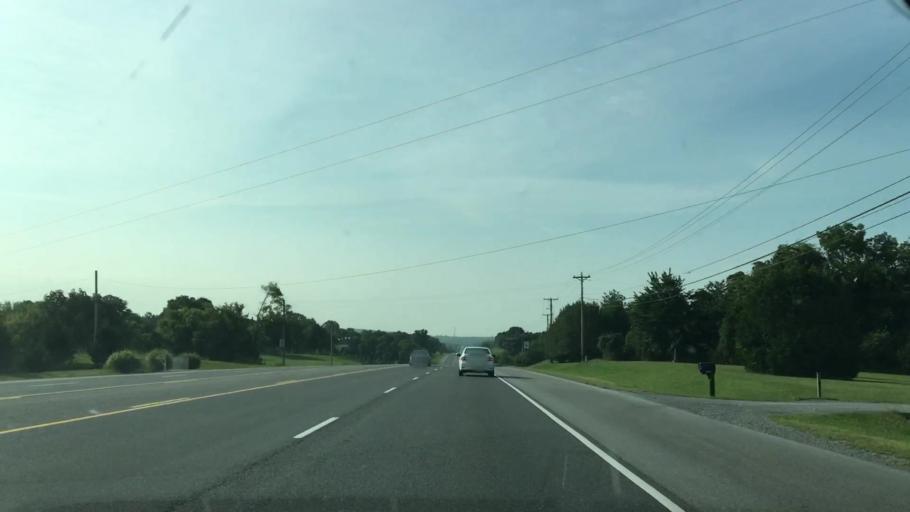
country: US
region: Tennessee
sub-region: Wilson County
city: Mount Juliet
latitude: 36.2060
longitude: -86.4186
